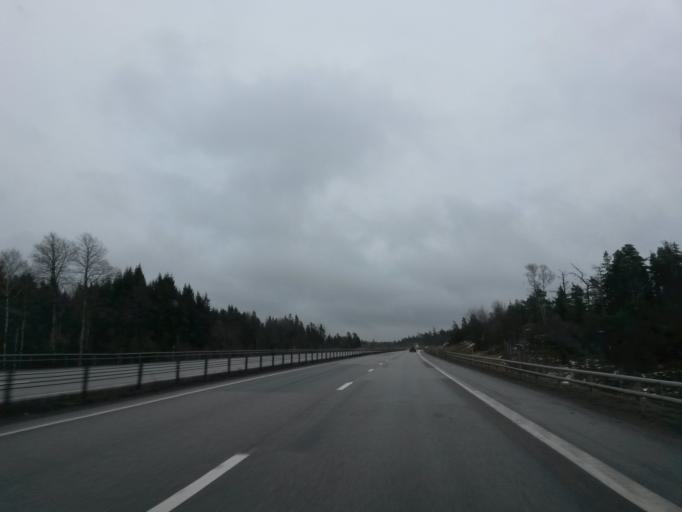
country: SE
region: Vaestra Goetaland
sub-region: Uddevalla Kommun
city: Uddevalla
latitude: 58.3312
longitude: 12.0203
